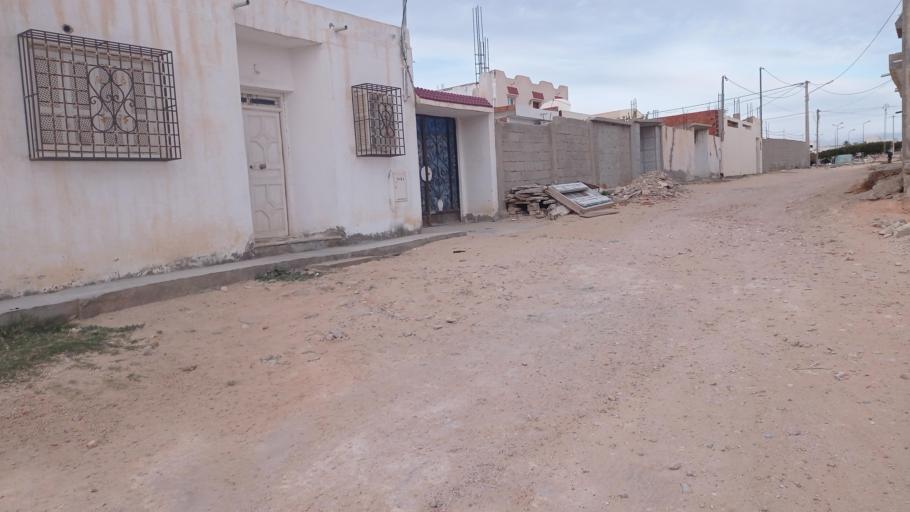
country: TN
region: Qabis
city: Gabes
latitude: 33.8370
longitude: 10.1142
